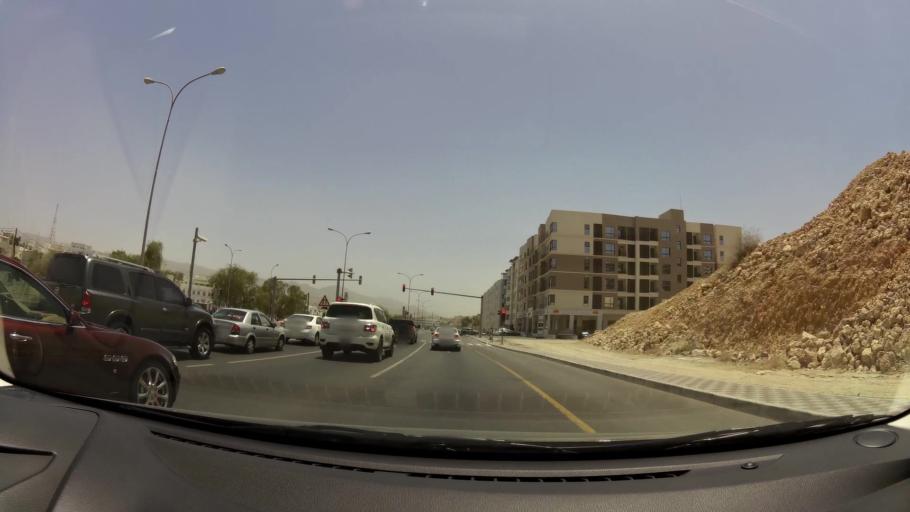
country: OM
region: Muhafazat Masqat
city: Muscat
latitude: 23.6214
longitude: 58.5034
